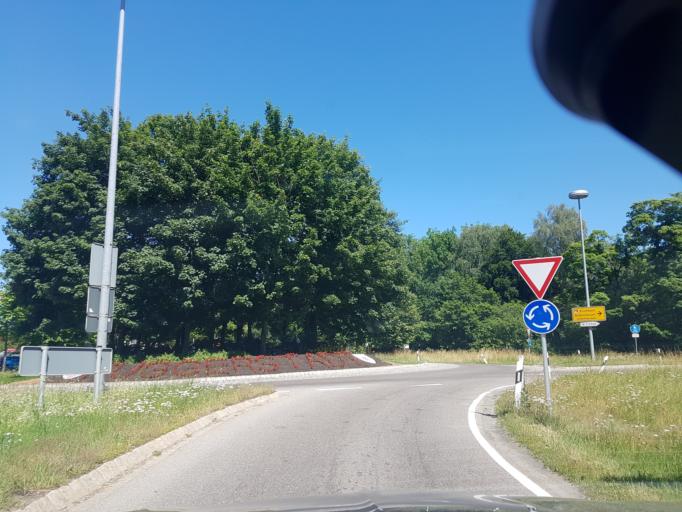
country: DE
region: Bavaria
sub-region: Swabia
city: Weissenhorn
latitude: 48.3012
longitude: 10.1531
